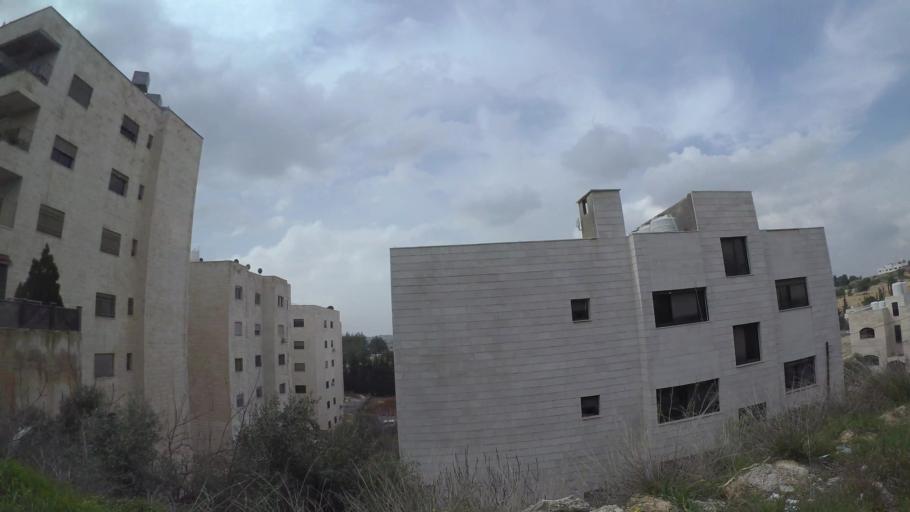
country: JO
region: Amman
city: Umm as Summaq
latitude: 31.8965
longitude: 35.8632
